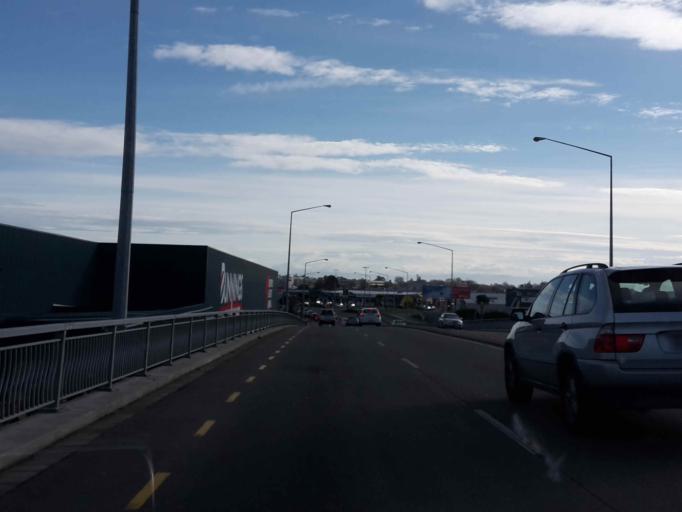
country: NZ
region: Canterbury
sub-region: Christchurch City
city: Christchurch
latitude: -43.5389
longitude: 172.6093
